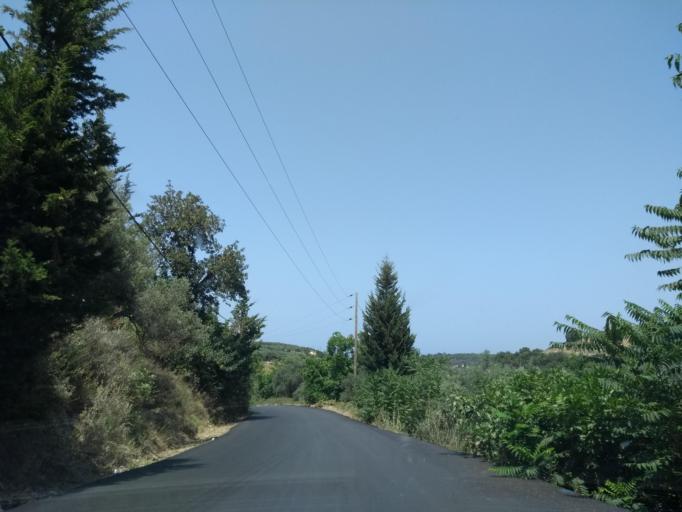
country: GR
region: Crete
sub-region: Nomos Chanias
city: Georgioupolis
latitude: 35.3178
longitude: 24.2990
